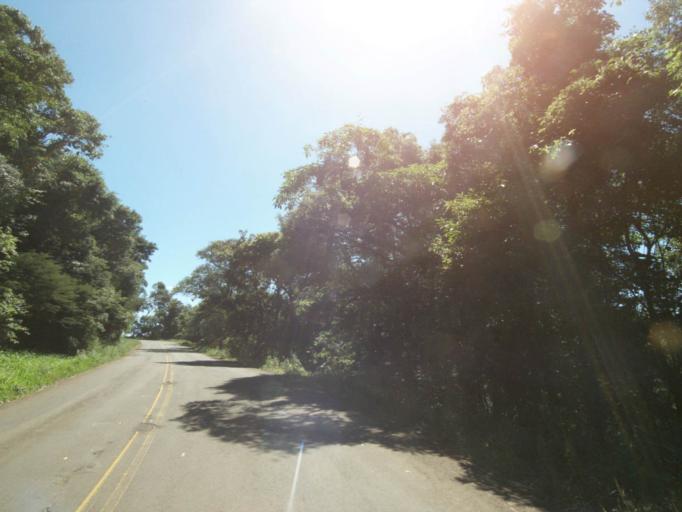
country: AR
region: Misiones
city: Bernardo de Irigoyen
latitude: -26.1873
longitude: -53.3638
